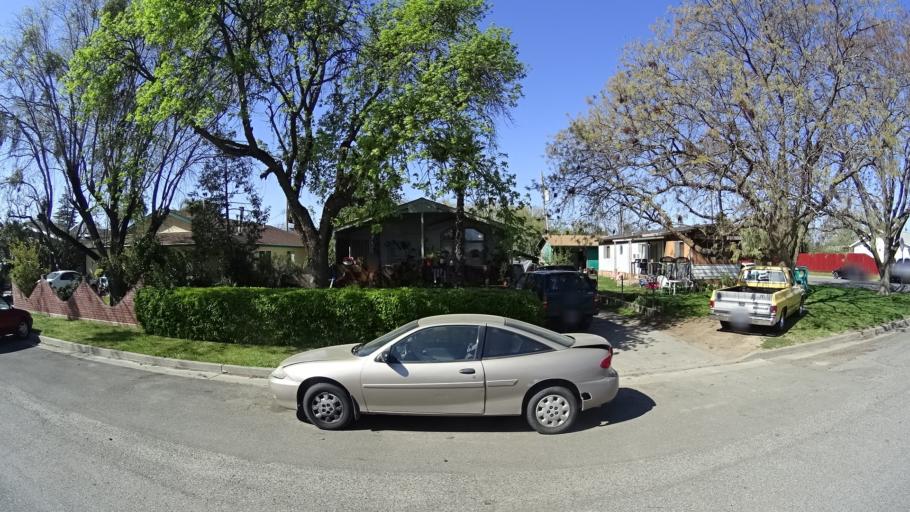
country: US
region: California
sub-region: Glenn County
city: Hamilton City
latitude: 39.7443
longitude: -122.0133
